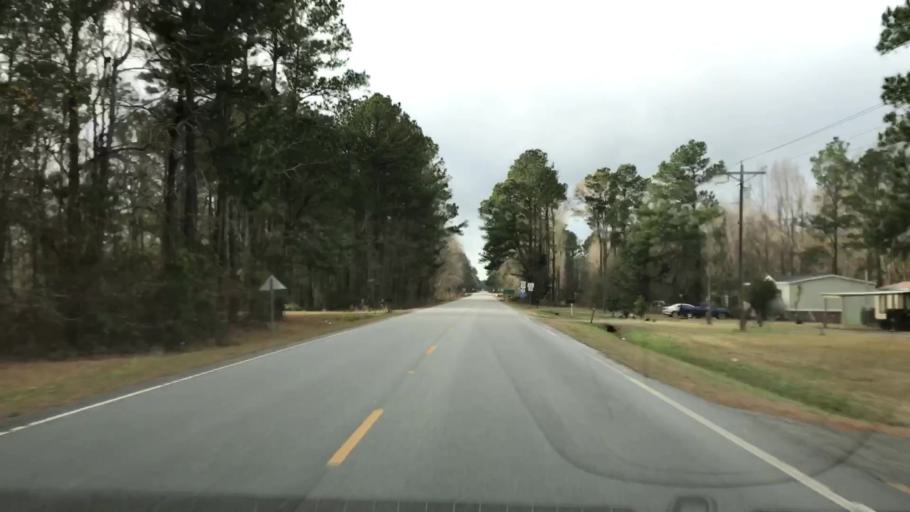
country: US
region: South Carolina
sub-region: Berkeley County
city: Saint Stephen
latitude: 33.2857
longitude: -79.7530
